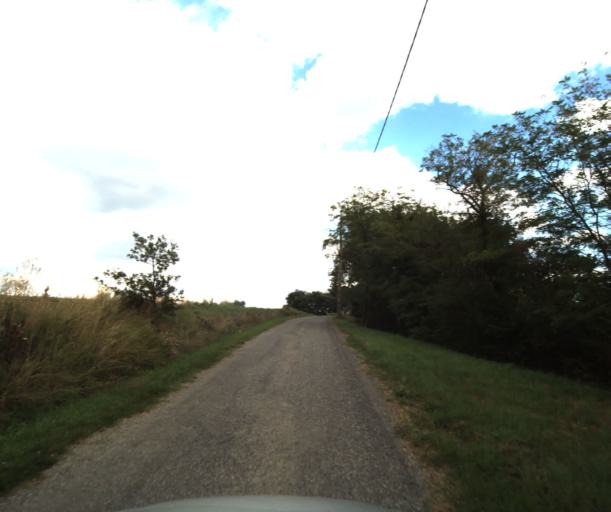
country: FR
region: Midi-Pyrenees
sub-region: Departement de la Haute-Garonne
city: Eaunes
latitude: 43.4181
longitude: 1.3592
